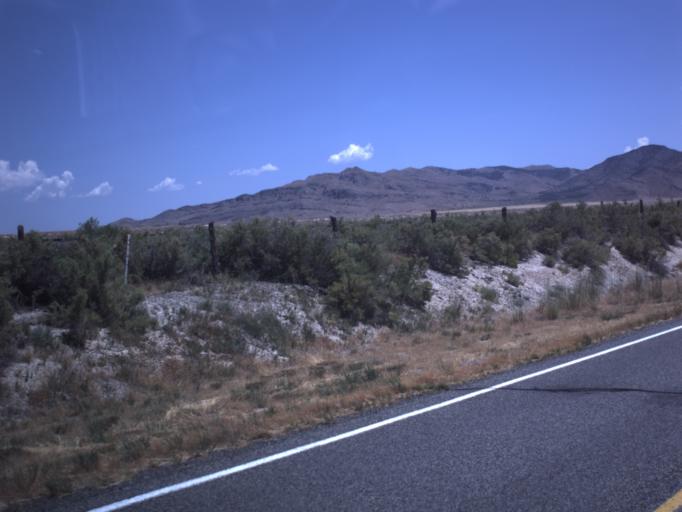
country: US
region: Utah
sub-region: Millard County
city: Delta
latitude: 39.5299
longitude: -112.3414
